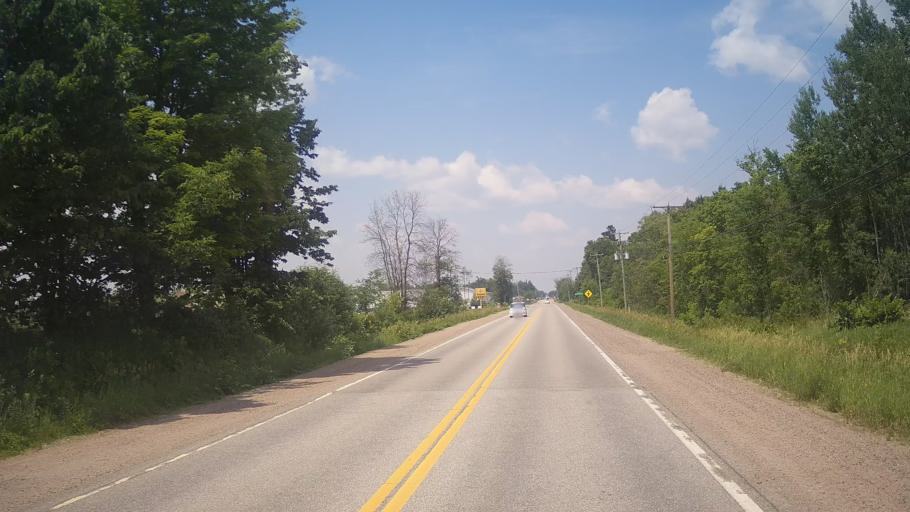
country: CA
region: Quebec
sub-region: Outaouais
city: Shawville
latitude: 45.6019
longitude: -76.4997
